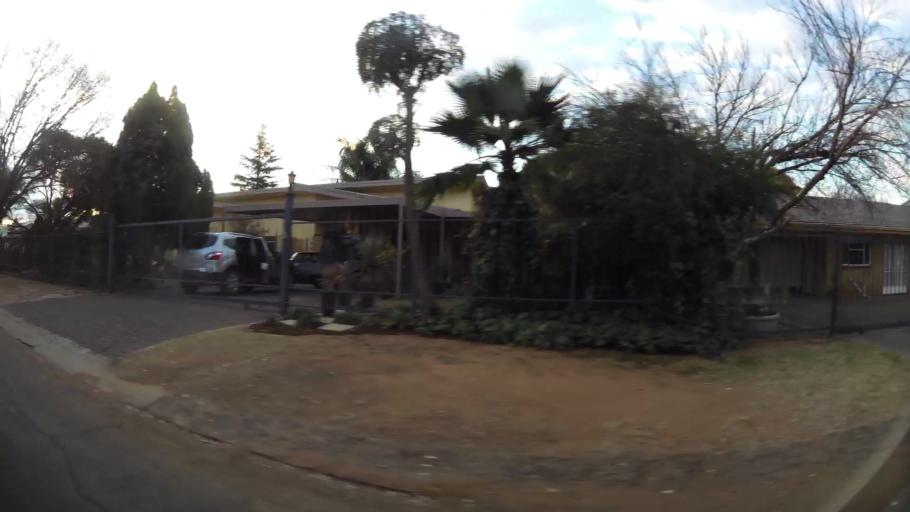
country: ZA
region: Orange Free State
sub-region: Mangaung Metropolitan Municipality
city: Bloemfontein
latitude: -29.1367
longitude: 26.1735
